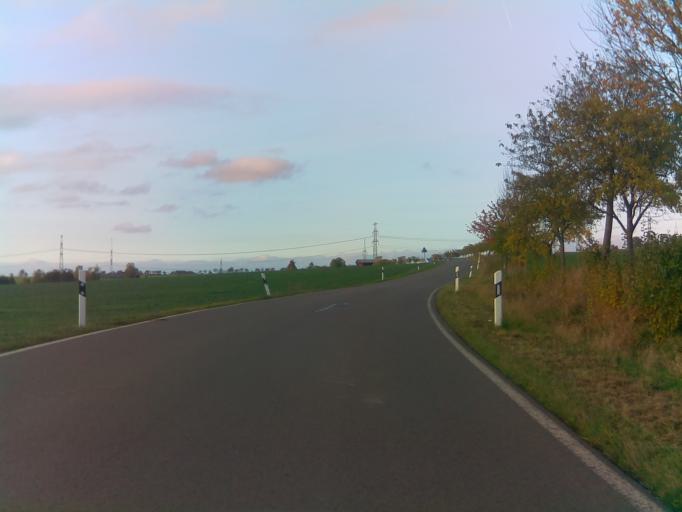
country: DE
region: Thuringia
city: Elleben
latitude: 50.8728
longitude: 11.0834
